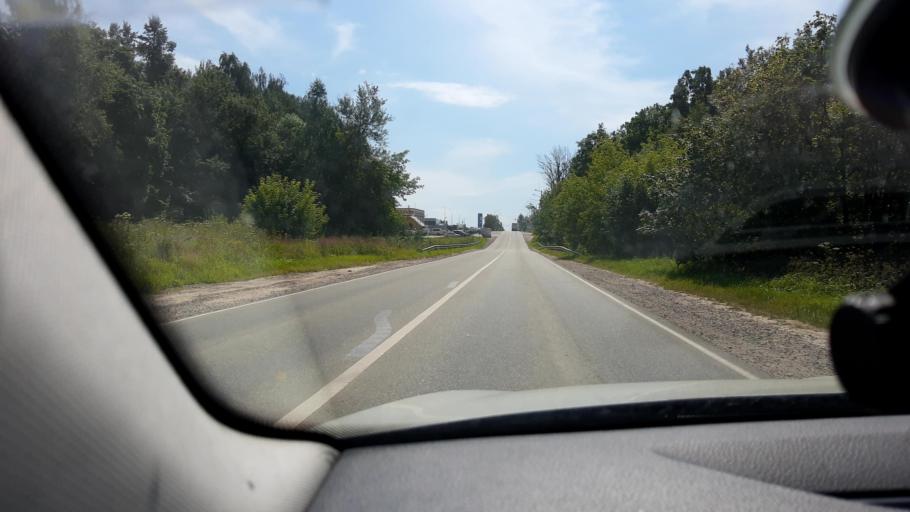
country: RU
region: Tula
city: Zaokskiy
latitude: 54.7515
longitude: 37.4386
